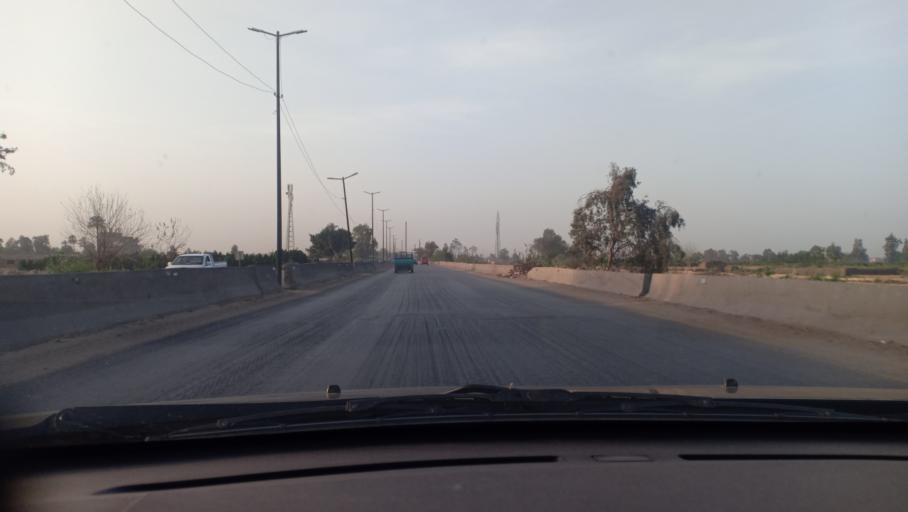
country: EG
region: Muhafazat al Minufiyah
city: Quwaysina
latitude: 30.5919
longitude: 31.2738
